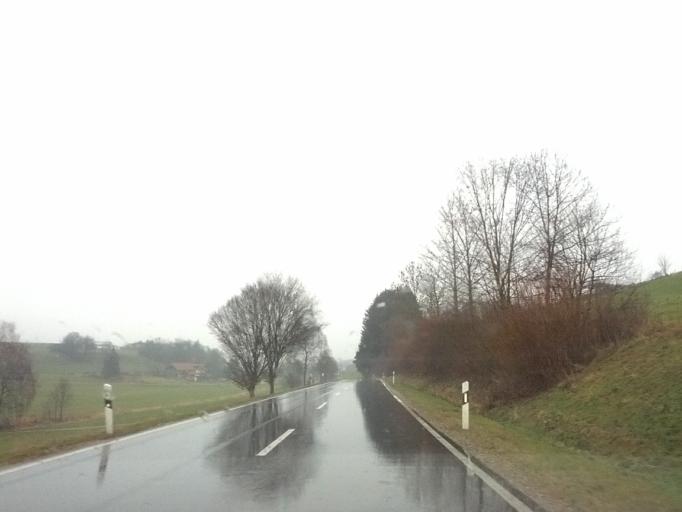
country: DE
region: Baden-Wuerttemberg
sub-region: Tuebingen Region
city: Steinhausen an der Rottum
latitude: 47.9947
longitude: 9.9897
